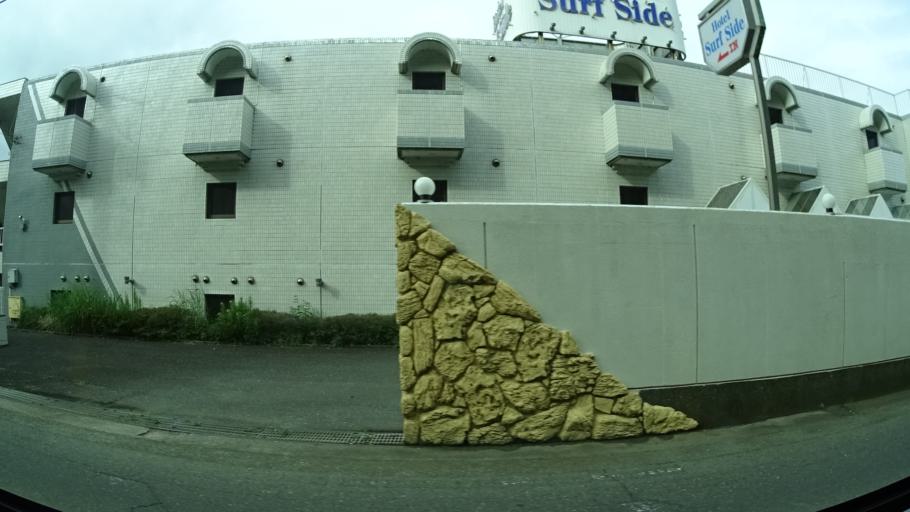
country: JP
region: Kanagawa
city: Miura
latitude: 35.1714
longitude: 139.6593
